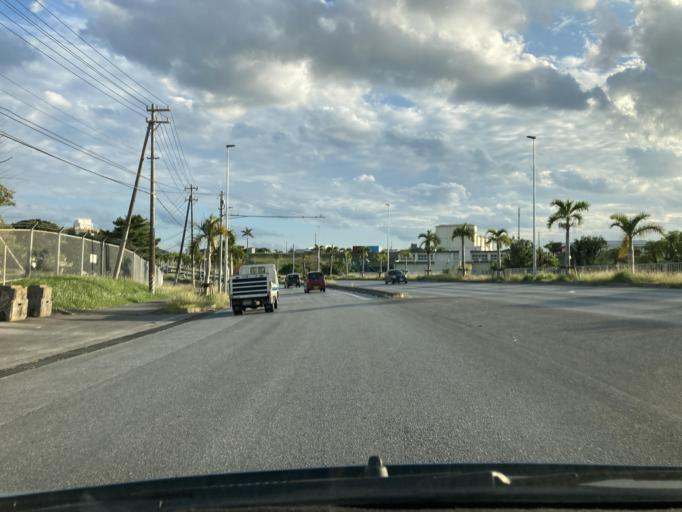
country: JP
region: Okinawa
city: Chatan
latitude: 26.3041
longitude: 127.7793
